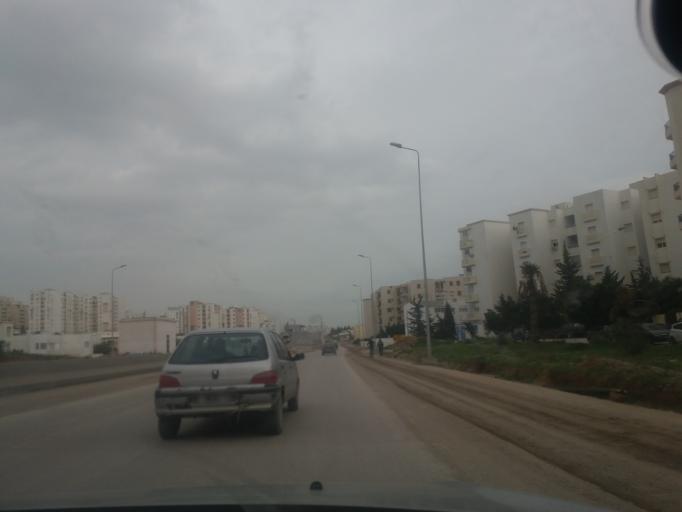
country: TN
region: Tunis
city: Tunis
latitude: 36.8550
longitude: 10.1500
